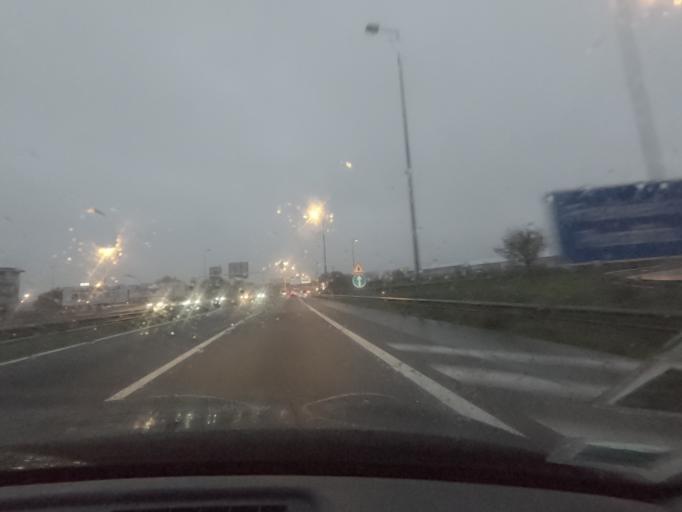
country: PT
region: Porto
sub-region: Matosinhos
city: Santa Cruz do Bispo
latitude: 41.2194
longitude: -8.6914
